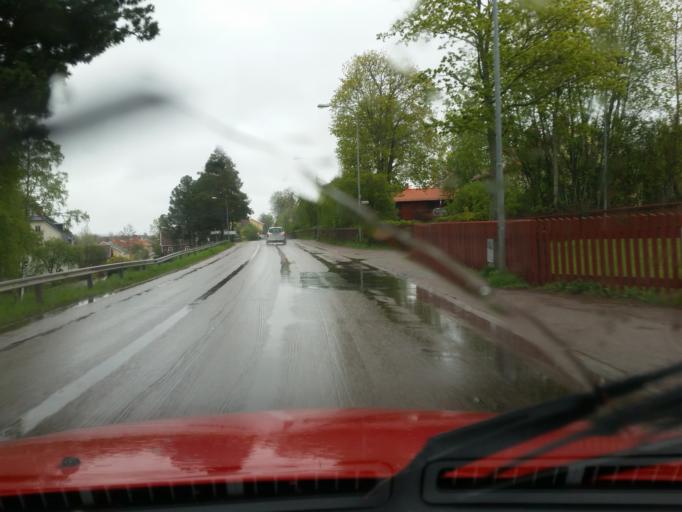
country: SE
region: Dalarna
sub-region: Hedemora Kommun
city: Hedemora
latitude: 60.2835
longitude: 15.9777
